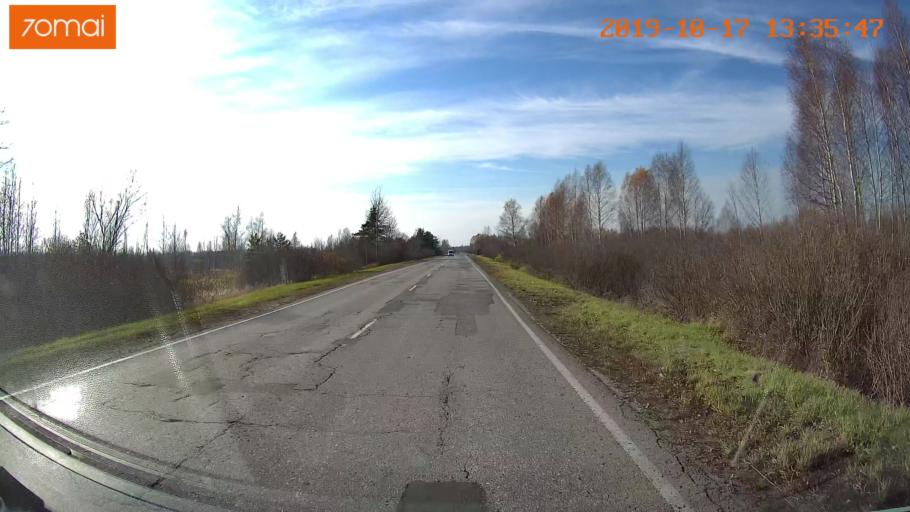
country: RU
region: Vladimir
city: Velikodvorskiy
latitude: 55.1413
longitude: 40.6807
